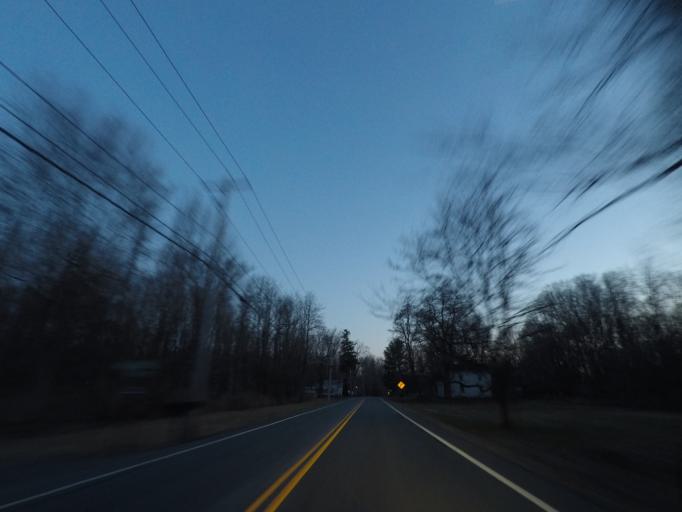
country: US
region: New York
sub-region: Schenectady County
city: Niskayuna
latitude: 42.8010
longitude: -73.8263
